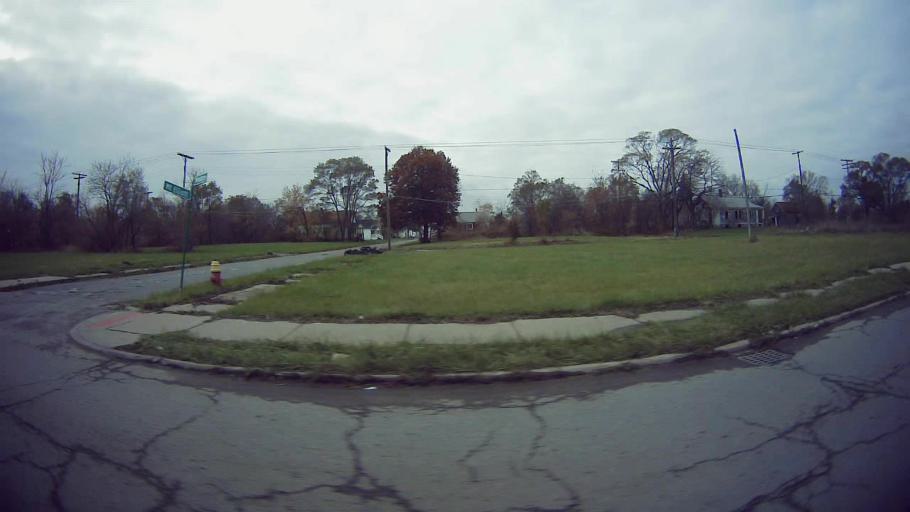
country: US
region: Michigan
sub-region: Wayne County
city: Hamtramck
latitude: 42.3968
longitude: -83.0376
